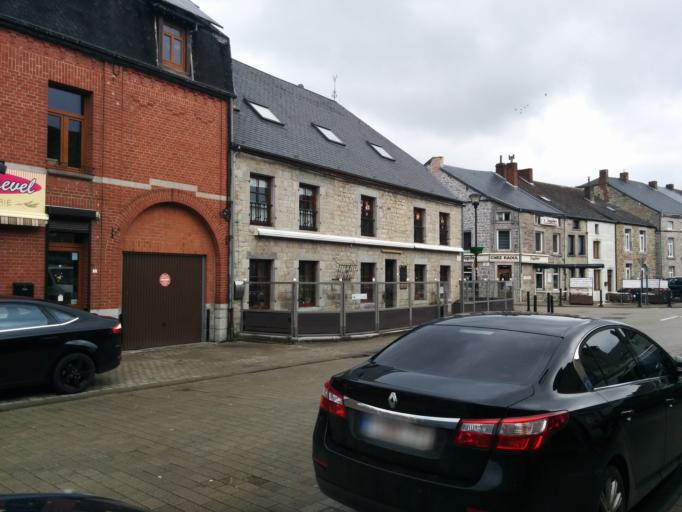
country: BE
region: Wallonia
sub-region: Province de Namur
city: Couvin
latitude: 50.0739
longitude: 4.6066
